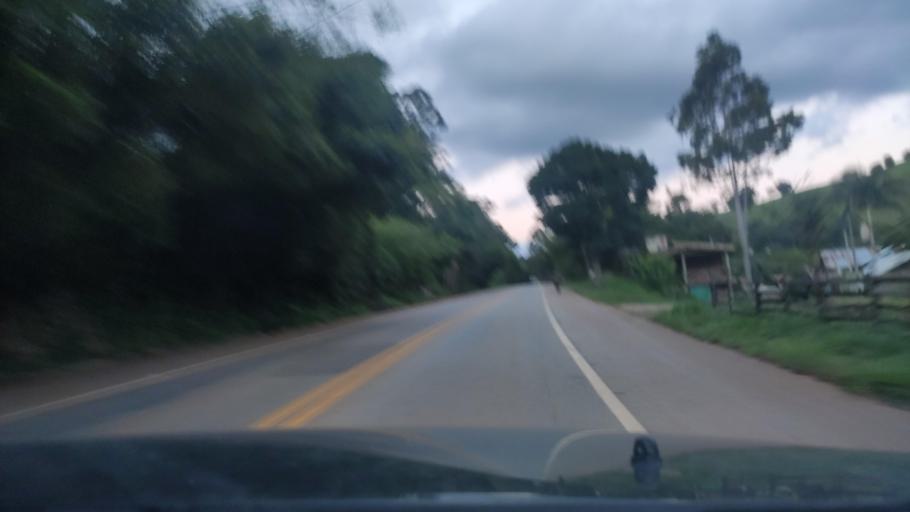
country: BR
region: Sao Paulo
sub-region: Campos Do Jordao
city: Campos do Jordao
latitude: -22.8043
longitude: -45.7512
